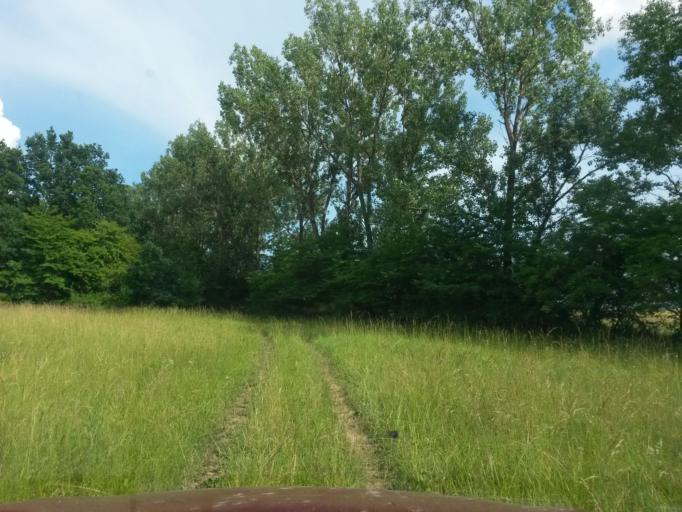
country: SK
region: Kosicky
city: Moldava nad Bodvou
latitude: 48.6201
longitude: 21.1000
